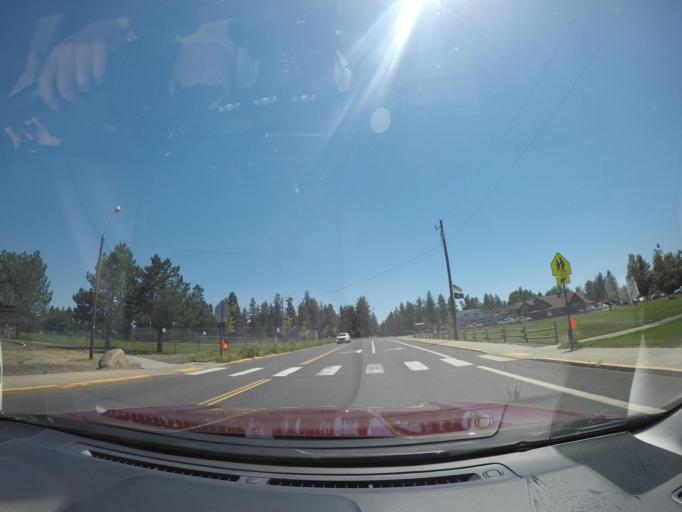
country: US
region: Oregon
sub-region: Deschutes County
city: Sisters
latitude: 44.2911
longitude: -121.5437
